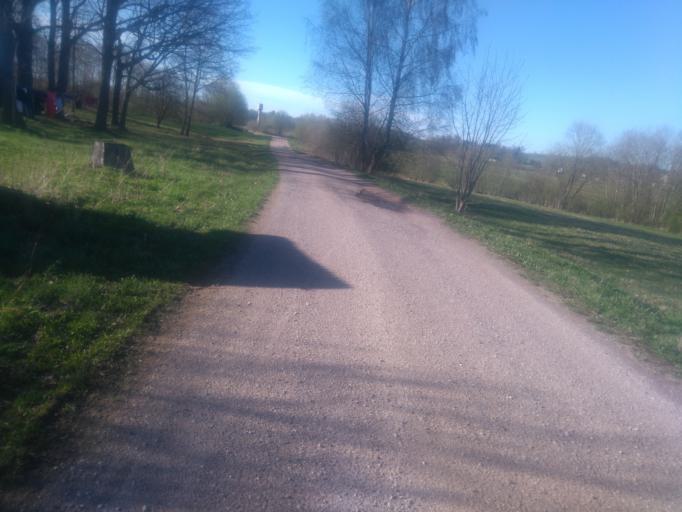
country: LV
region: Vecpiebalga
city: Vecpiebalga
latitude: 57.0190
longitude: 25.8522
